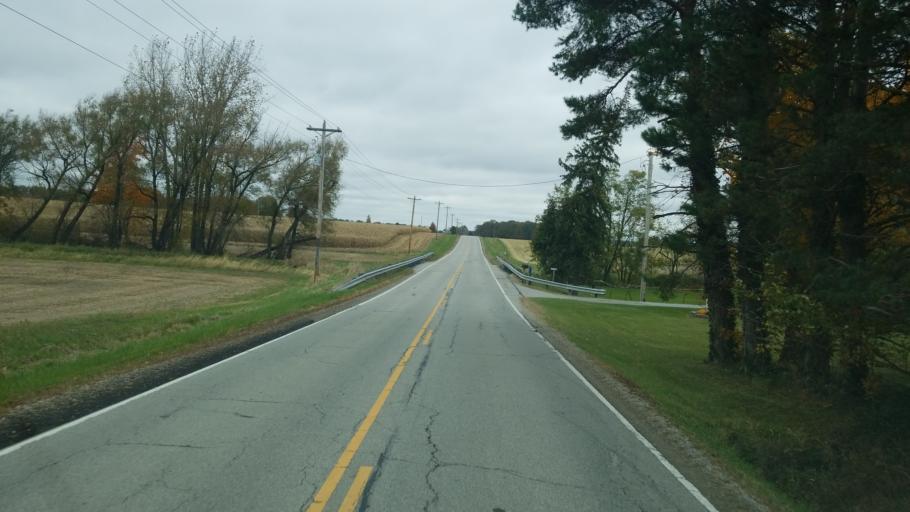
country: US
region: Ohio
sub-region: Huron County
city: Willard
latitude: 40.9852
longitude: -82.8533
